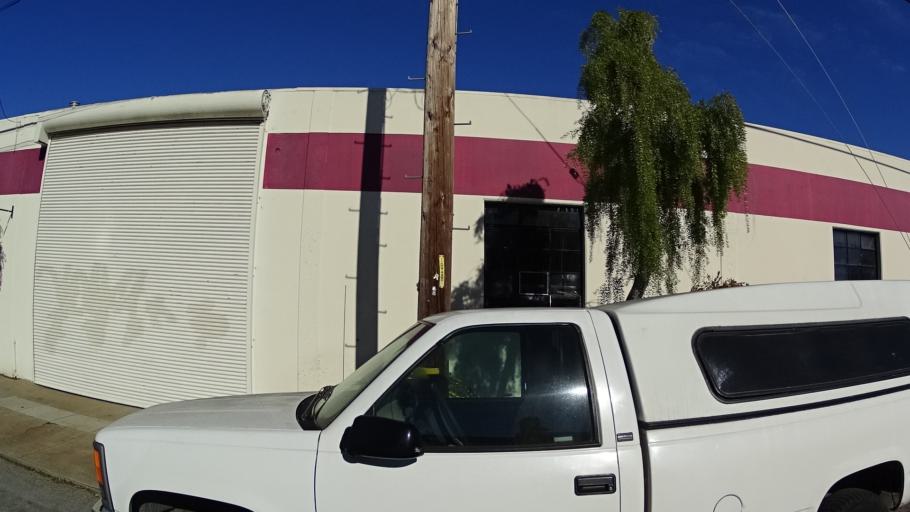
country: US
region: California
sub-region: San Mateo County
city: San Mateo
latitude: 37.5854
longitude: -122.3335
